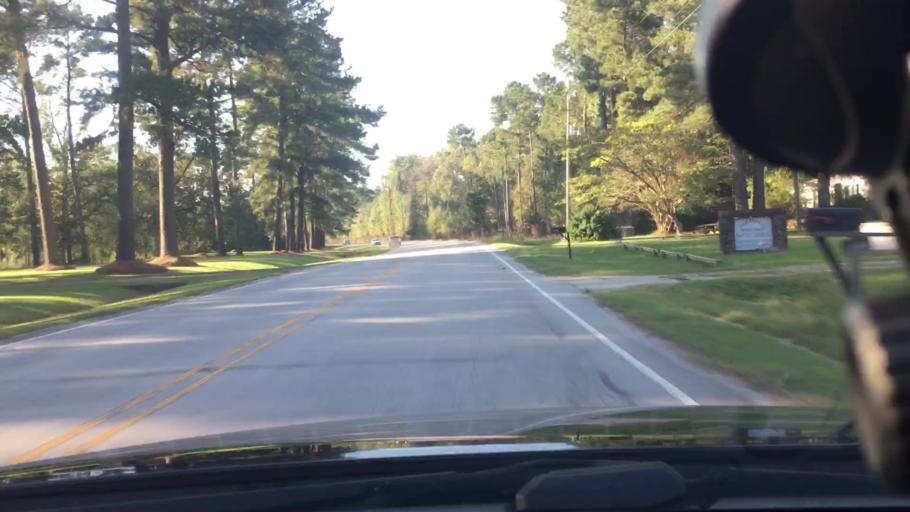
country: US
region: North Carolina
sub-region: Craven County
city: Vanceboro
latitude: 35.4084
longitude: -77.2442
